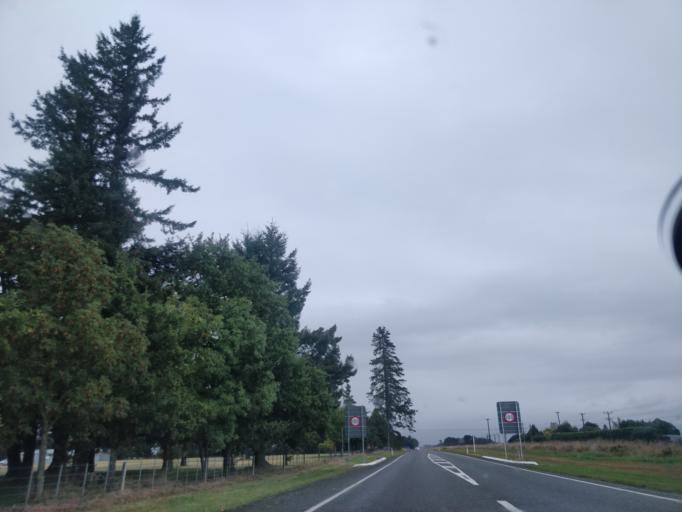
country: NZ
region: Canterbury
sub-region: Selwyn District
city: Darfield
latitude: -43.3857
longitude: 172.0140
